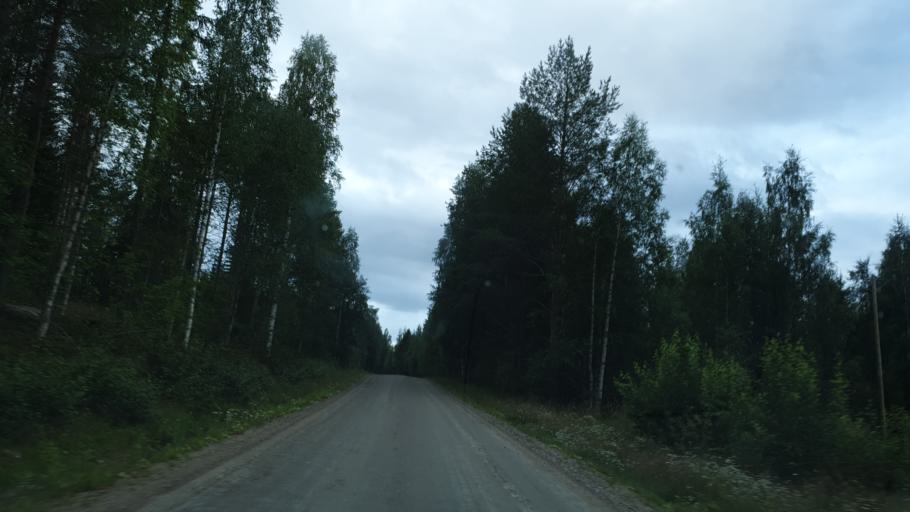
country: FI
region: Kainuu
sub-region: Kehys-Kainuu
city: Kuhmo
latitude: 64.1992
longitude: 29.3669
